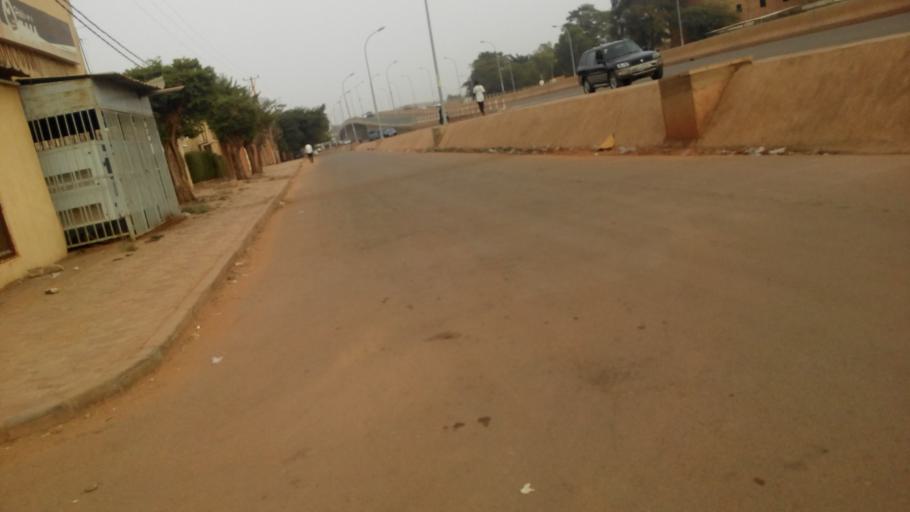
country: NE
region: Niamey
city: Niamey
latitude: 13.5342
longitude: 2.1053
